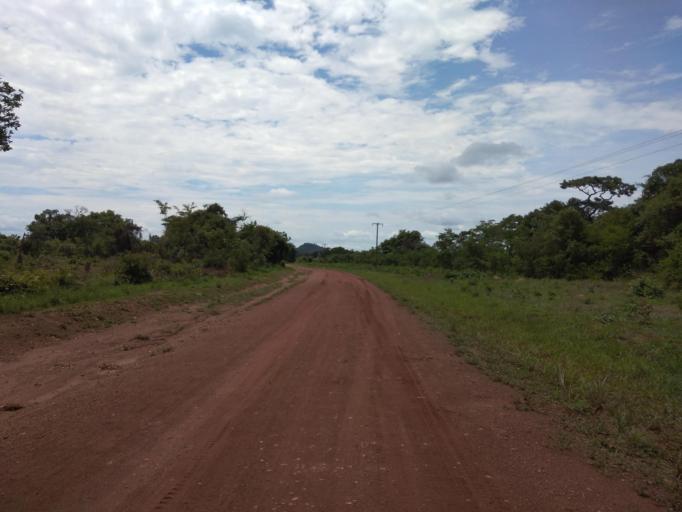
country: ZM
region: Copperbelt
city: Luanshya
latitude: -13.4810
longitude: 28.7558
